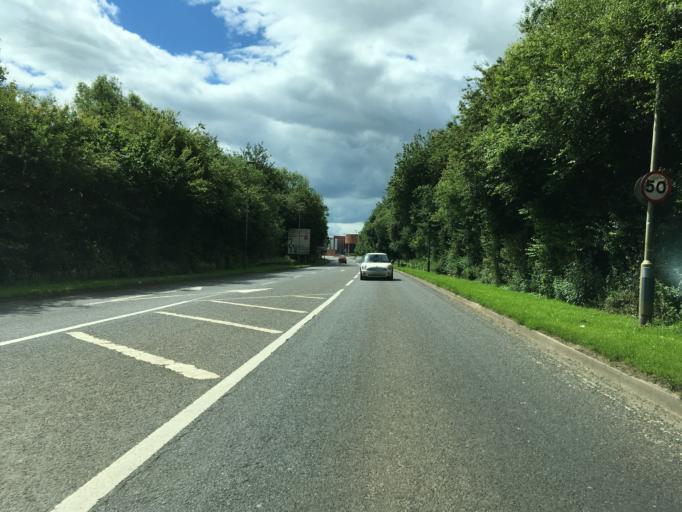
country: GB
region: England
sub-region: Oxfordshire
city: Banbury
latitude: 52.0680
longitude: -1.3311
